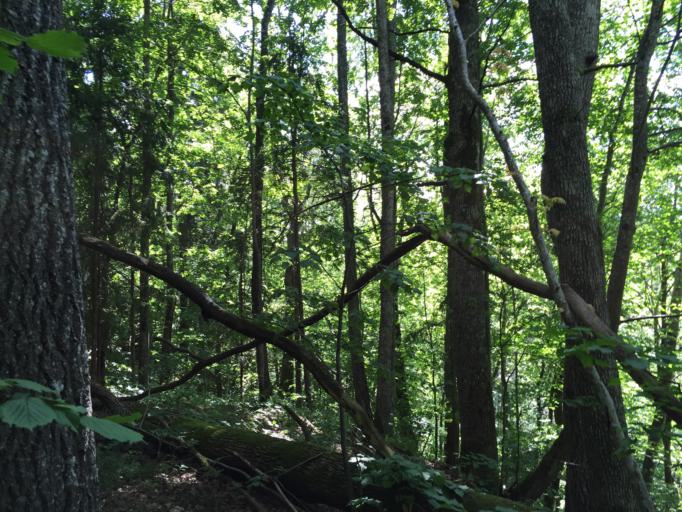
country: LV
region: Sigulda
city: Sigulda
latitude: 57.1874
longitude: 24.9331
